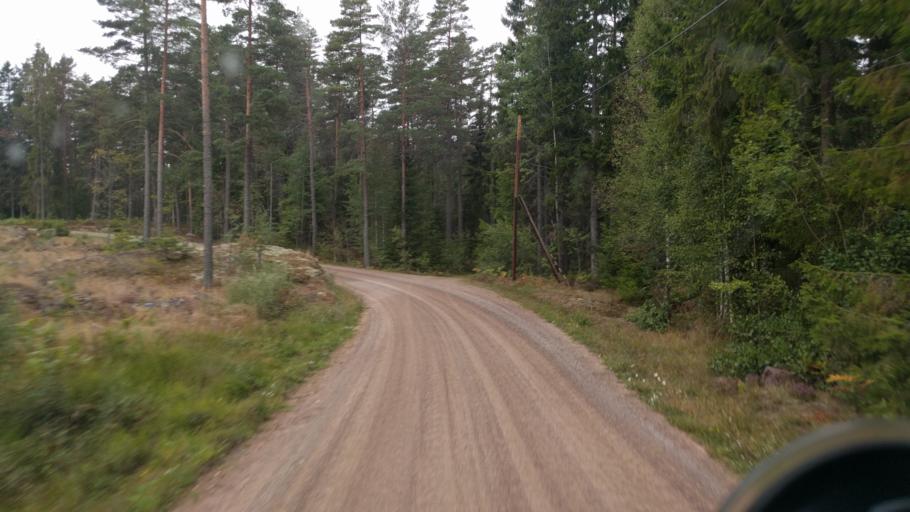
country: SE
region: Kalmar
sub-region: Vasterviks Kommun
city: Ankarsrum
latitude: 57.7511
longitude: 16.1798
